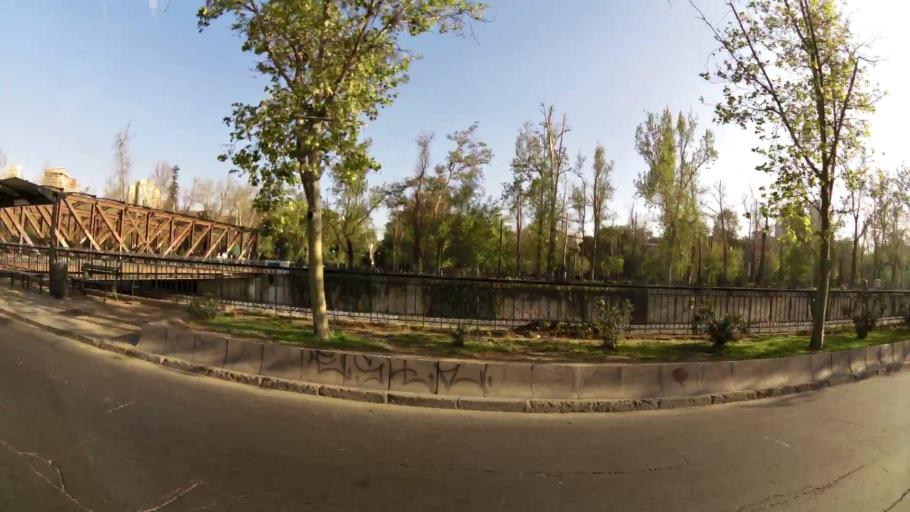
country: CL
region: Santiago Metropolitan
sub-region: Provincia de Santiago
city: Santiago
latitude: -33.4349
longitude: -70.6391
